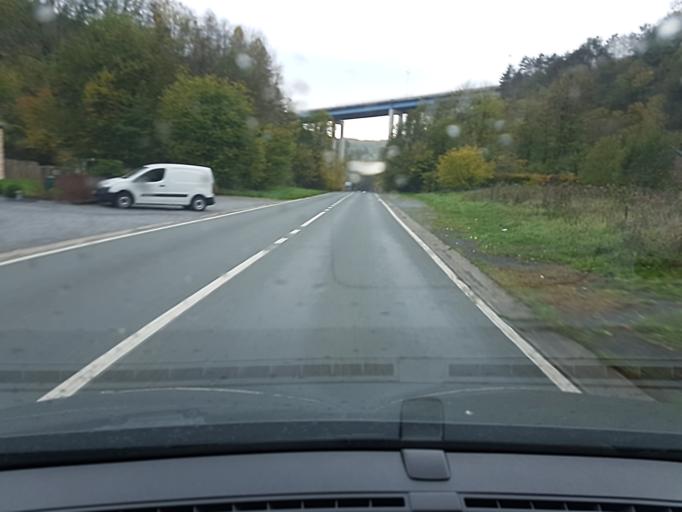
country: BE
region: Wallonia
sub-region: Province de Liege
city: Aywaille
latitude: 50.4856
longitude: 5.7196
